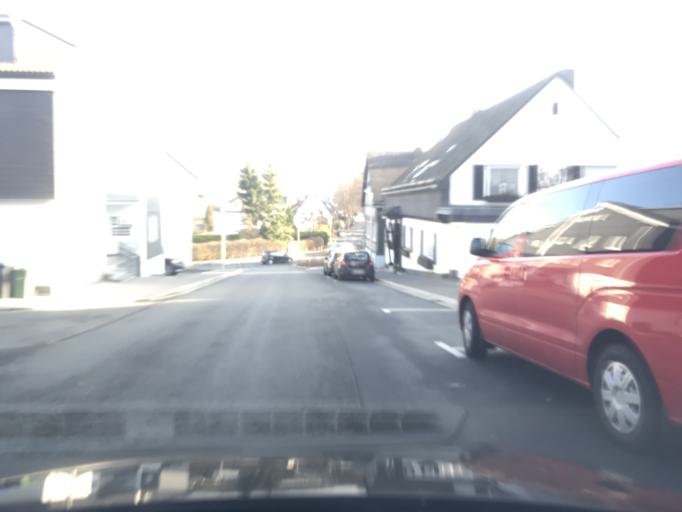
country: DE
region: North Rhine-Westphalia
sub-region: Regierungsbezirk Arnsberg
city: Brilon
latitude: 51.3908
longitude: 8.5708
